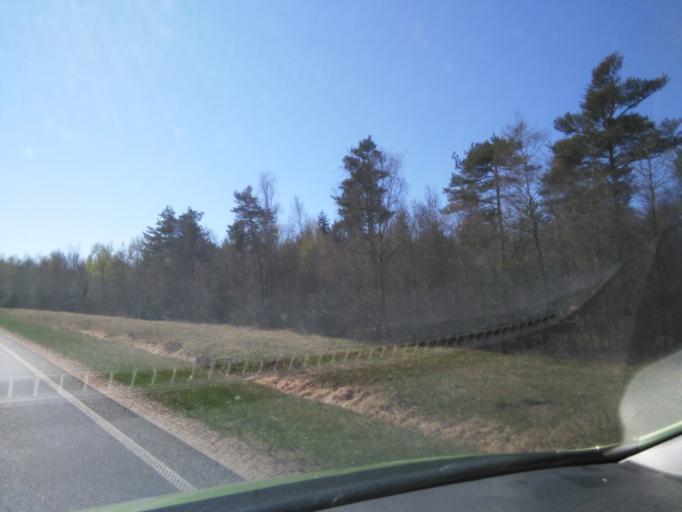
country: DK
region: South Denmark
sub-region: Varde Kommune
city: Oksbol
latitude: 55.6020
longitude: 8.2246
